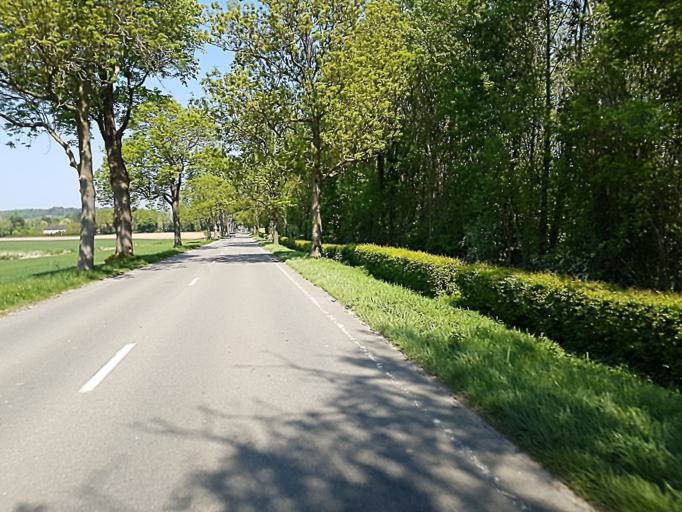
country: BE
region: Wallonia
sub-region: Province du Brabant Wallon
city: Grez-Doiceau
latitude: 50.7712
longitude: 4.7111
